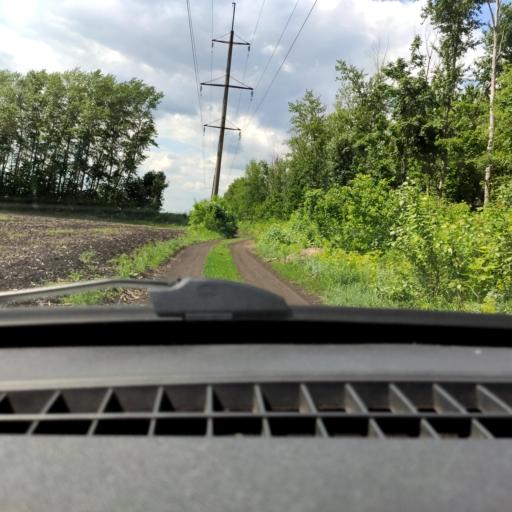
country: RU
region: Bashkortostan
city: Kabakovo
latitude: 54.5041
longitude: 56.1256
